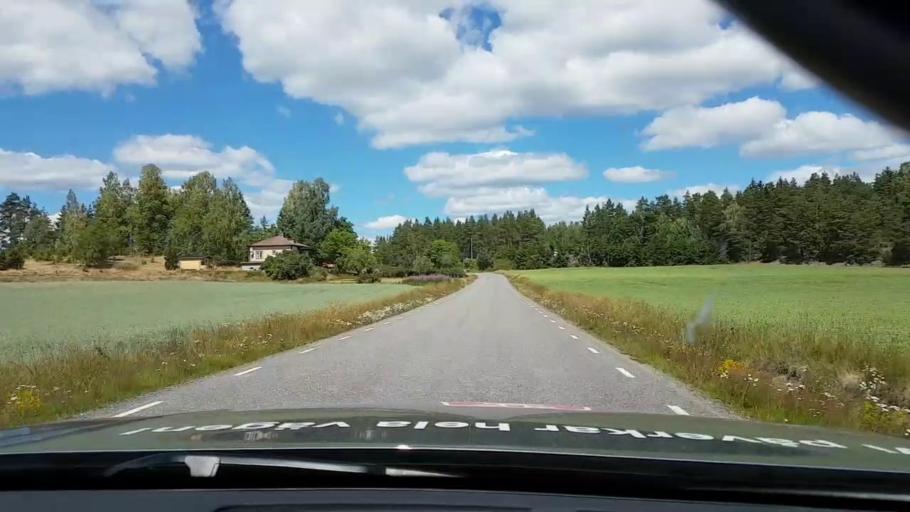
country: SE
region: Kalmar
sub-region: Vasterviks Kommun
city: Forserum
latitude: 58.0166
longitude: 16.5766
